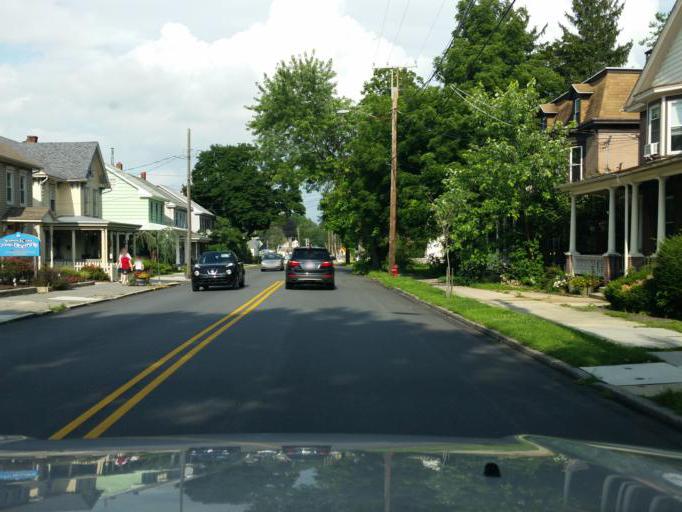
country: US
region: Pennsylvania
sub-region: Dauphin County
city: Hummelstown
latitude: 40.2657
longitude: -76.7018
